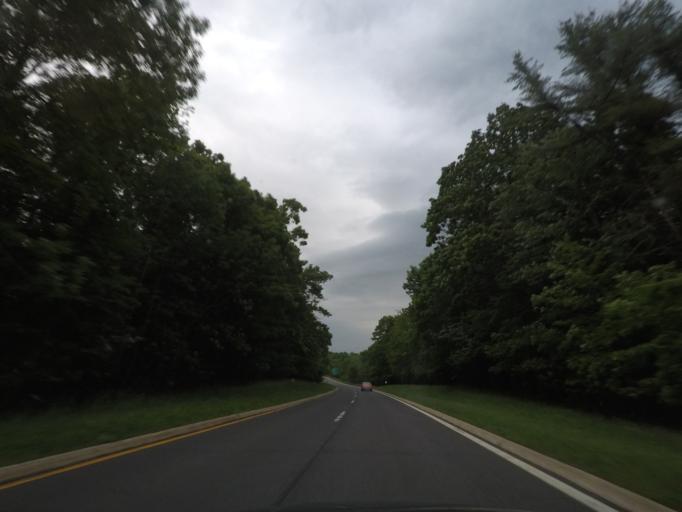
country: US
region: New York
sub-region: Columbia County
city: Philmont
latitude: 42.2497
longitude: -73.6158
